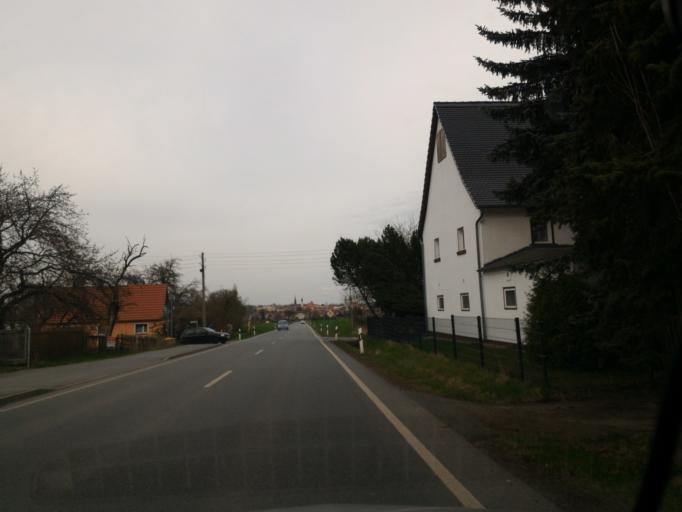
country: DE
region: Saxony
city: Olbersdorf
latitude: 50.8838
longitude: 14.7869
